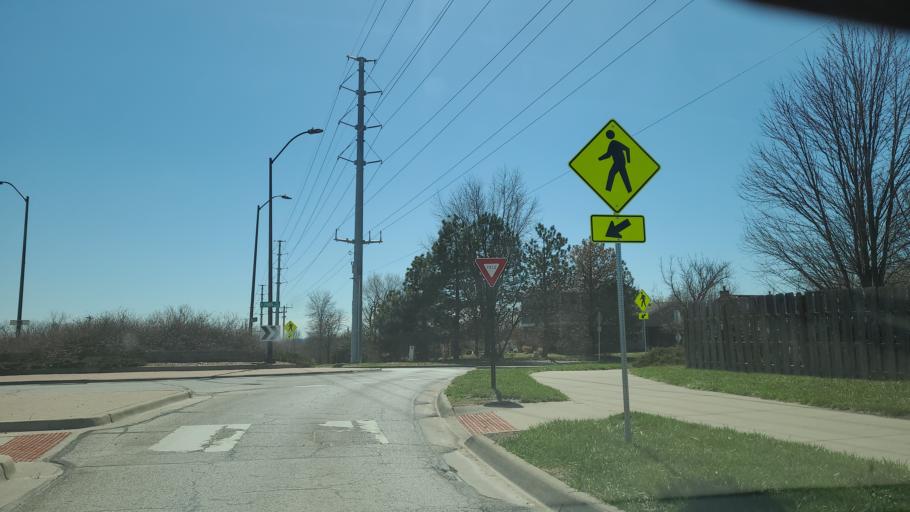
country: US
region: Kansas
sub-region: Douglas County
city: Lawrence
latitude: 38.9340
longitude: -95.2050
